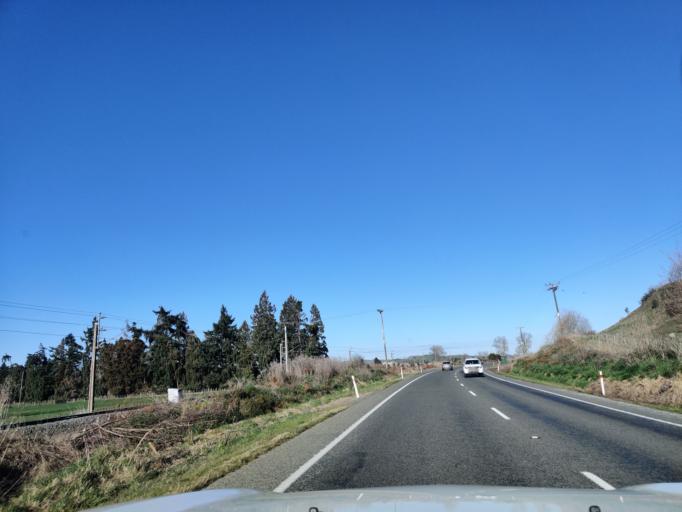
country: NZ
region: Manawatu-Wanganui
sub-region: Ruapehu District
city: Waiouru
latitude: -39.8461
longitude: 175.7391
